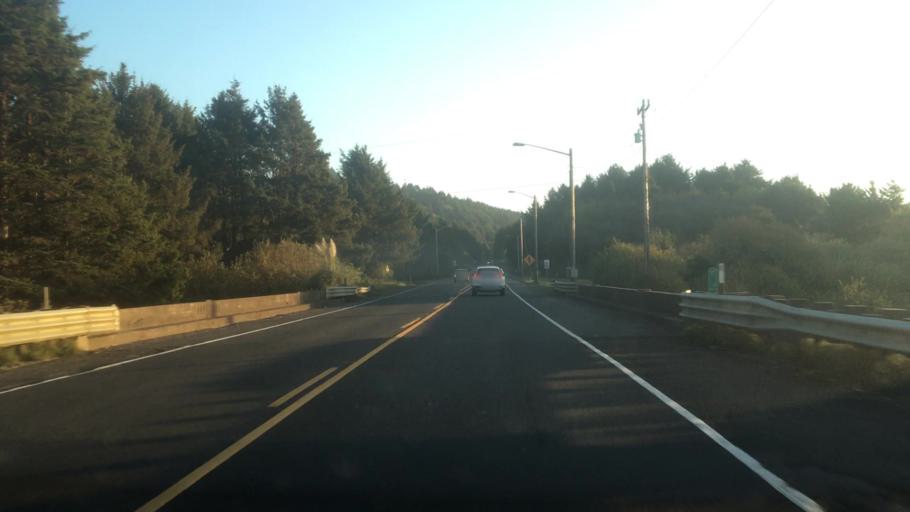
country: US
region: Oregon
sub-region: Clatsop County
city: Cannon Beach
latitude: 45.8725
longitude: -123.9582
